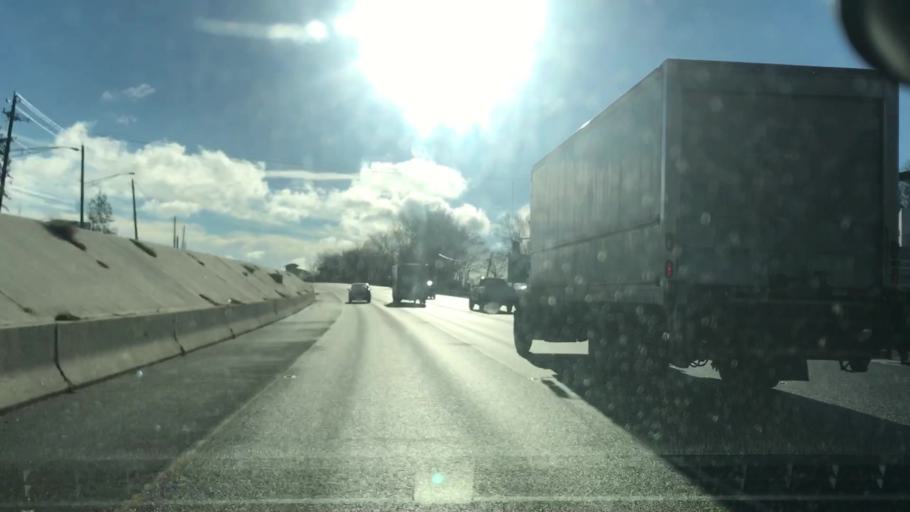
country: US
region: New Jersey
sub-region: Bergen County
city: Mahwah
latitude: 41.0775
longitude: -74.1482
